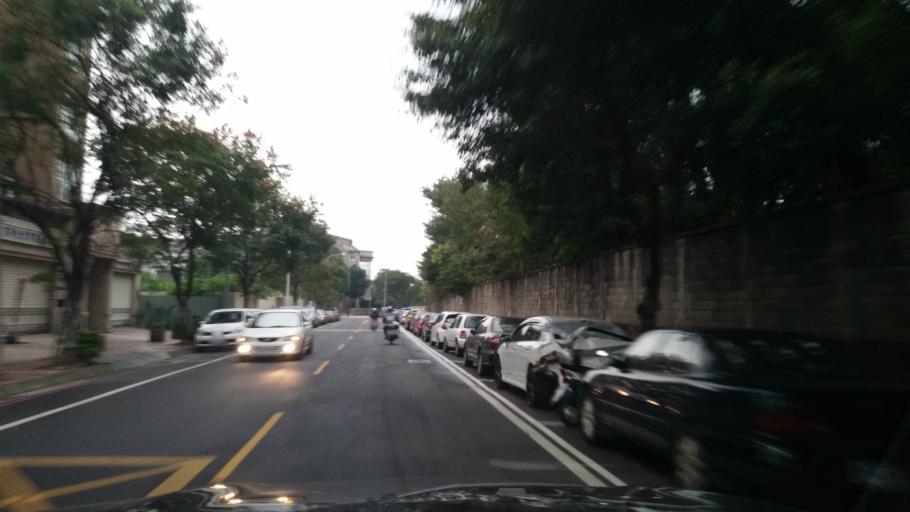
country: TW
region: Taiwan
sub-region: Taoyuan
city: Taoyuan
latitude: 25.0589
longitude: 121.3610
